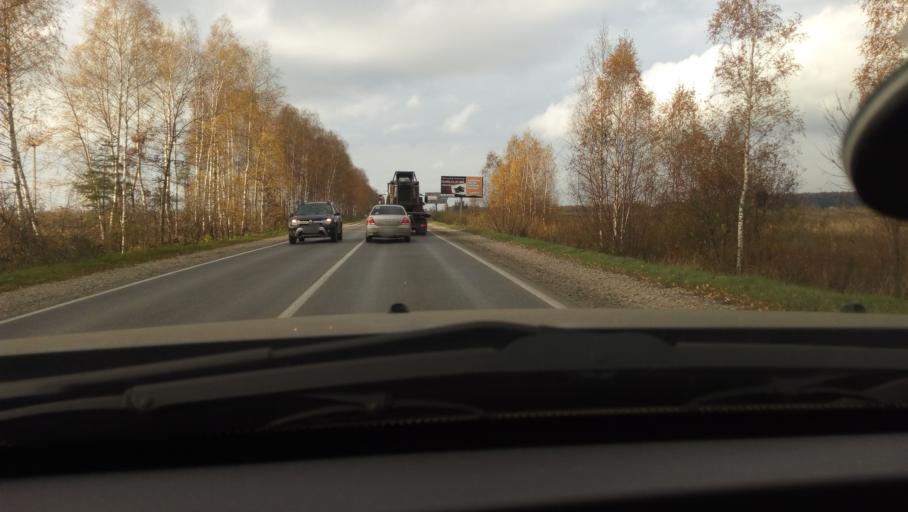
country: RU
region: Moskovskaya
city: Rakhmanovo
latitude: 55.7515
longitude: 38.6314
